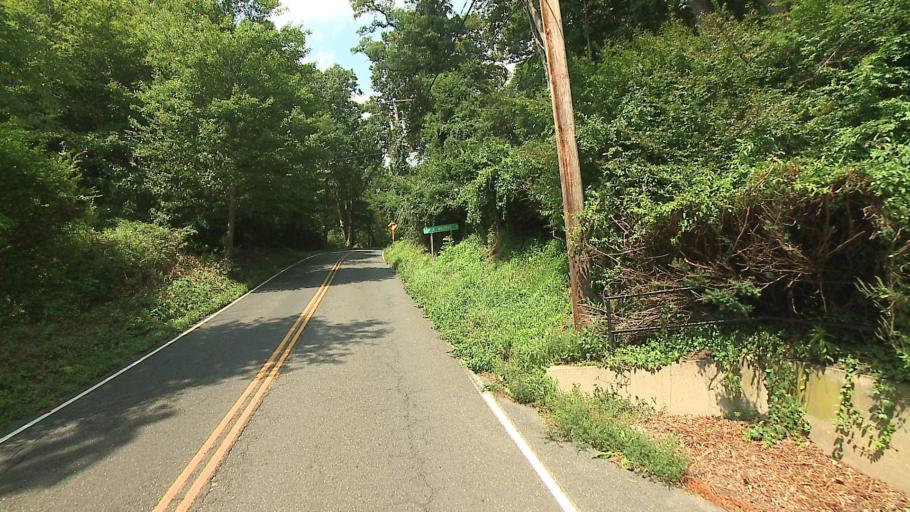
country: US
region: Connecticut
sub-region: Litchfield County
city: New Preston
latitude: 41.6416
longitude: -73.3203
